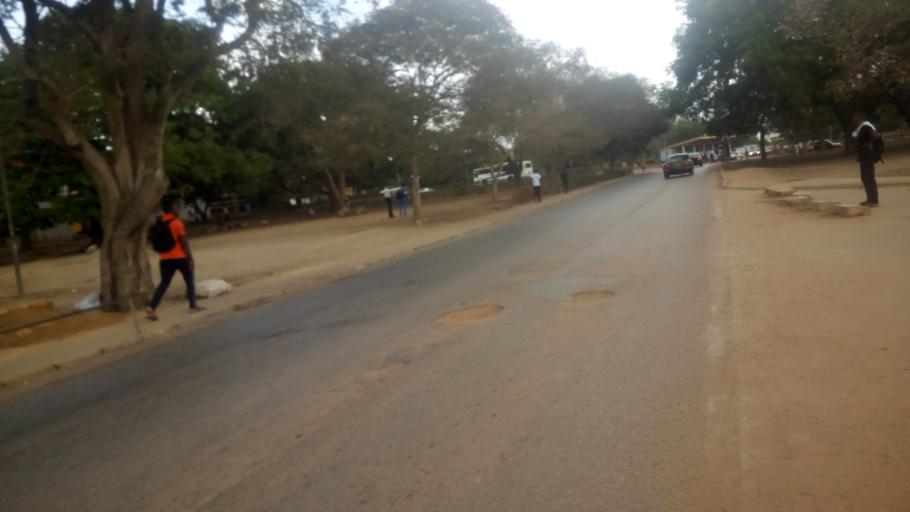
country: GH
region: Central
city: Cape Coast
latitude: 5.1152
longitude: -1.2920
